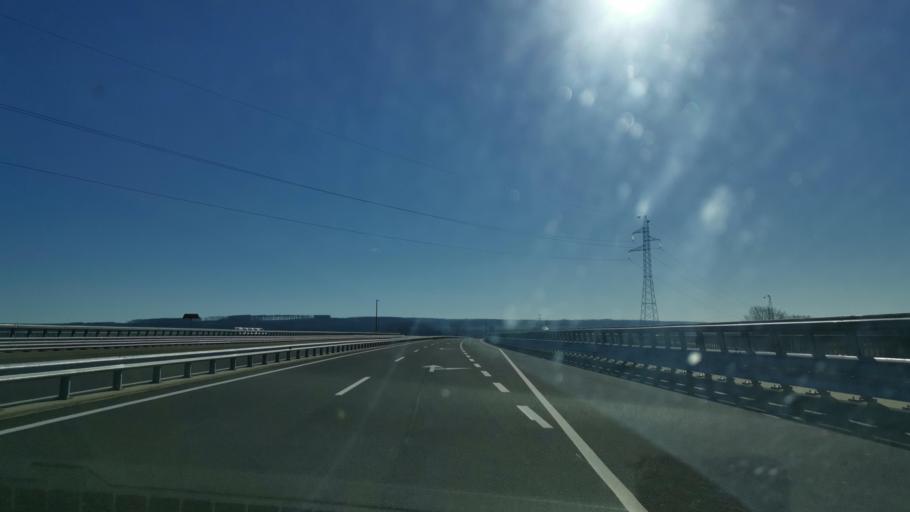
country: HU
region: Somogy
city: Balatonbereny
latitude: 46.6892
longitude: 17.2836
